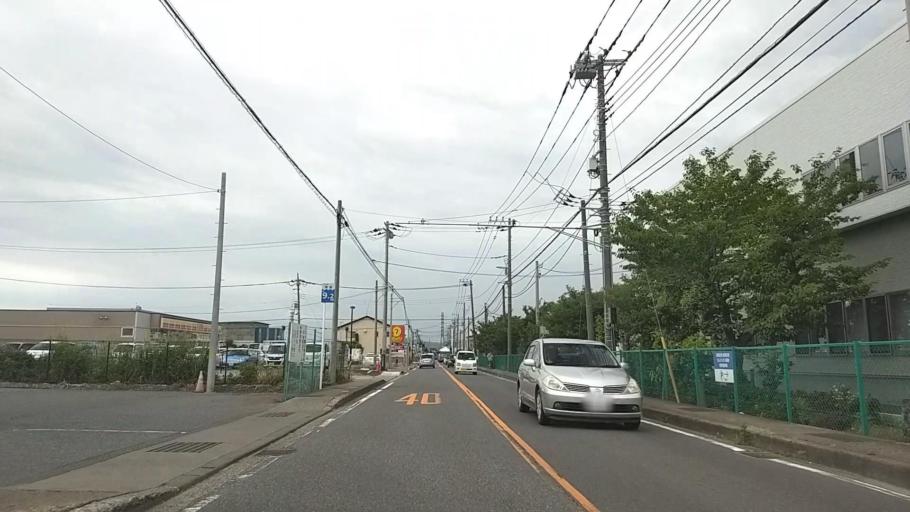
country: JP
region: Kanagawa
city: Isehara
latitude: 35.3760
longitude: 139.3583
